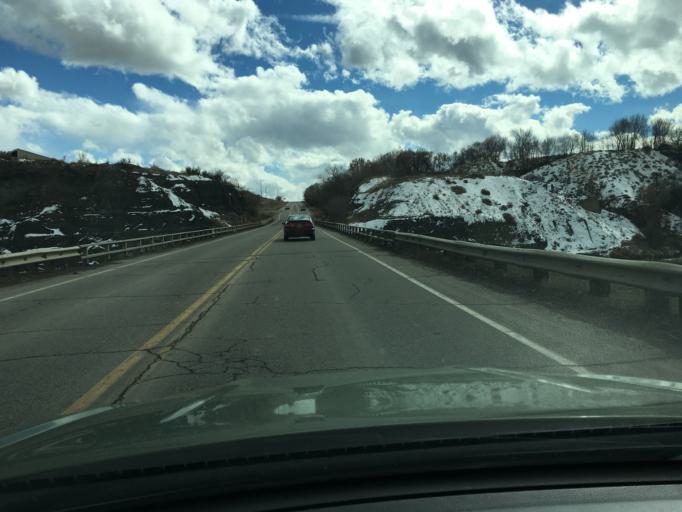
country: US
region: Colorado
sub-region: Mesa County
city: Clifton
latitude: 39.0556
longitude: -108.4595
